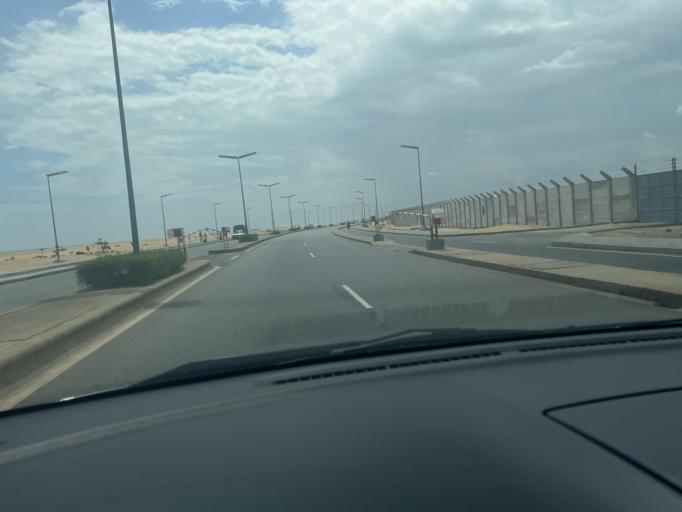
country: BJ
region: Littoral
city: Cotonou
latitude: 6.3484
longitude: 2.3761
